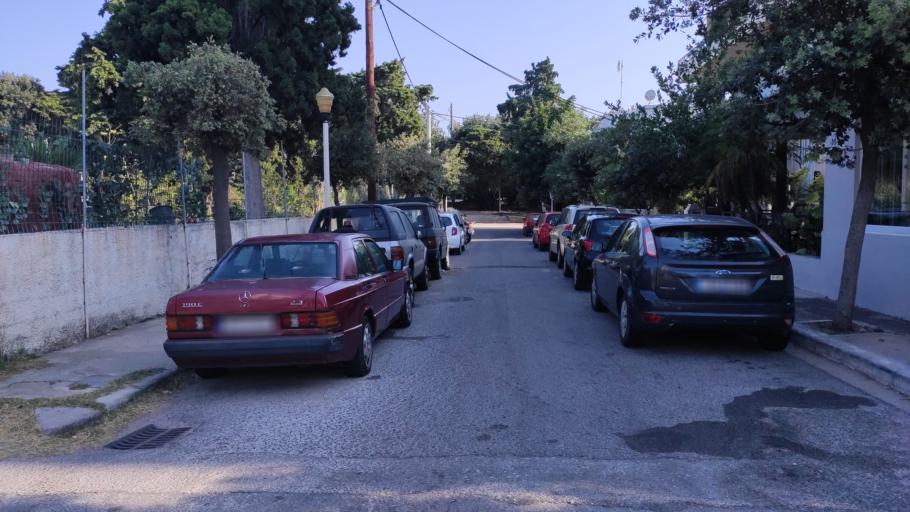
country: GR
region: South Aegean
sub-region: Nomos Dodekanisou
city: Rodos
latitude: 36.4393
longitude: 28.2317
